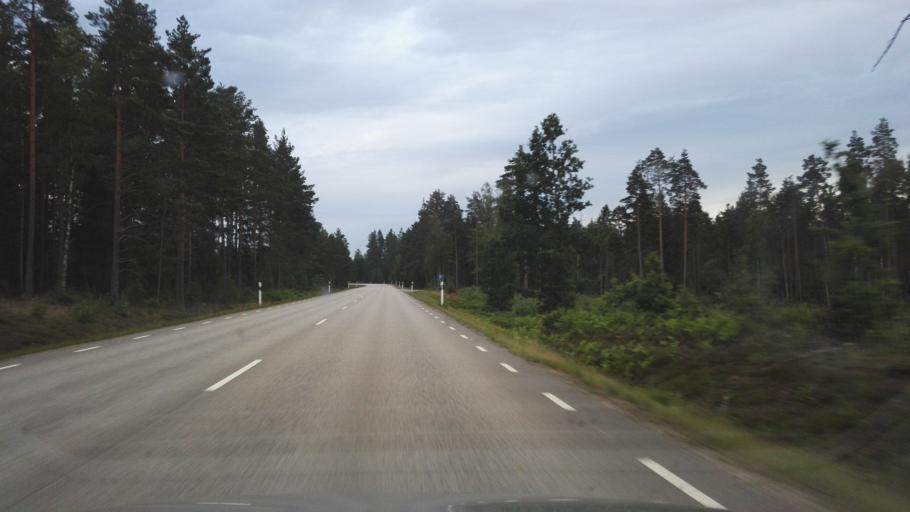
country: SE
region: Kronoberg
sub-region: Vaxjo Kommun
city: Braas
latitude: 57.0436
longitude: 15.0641
